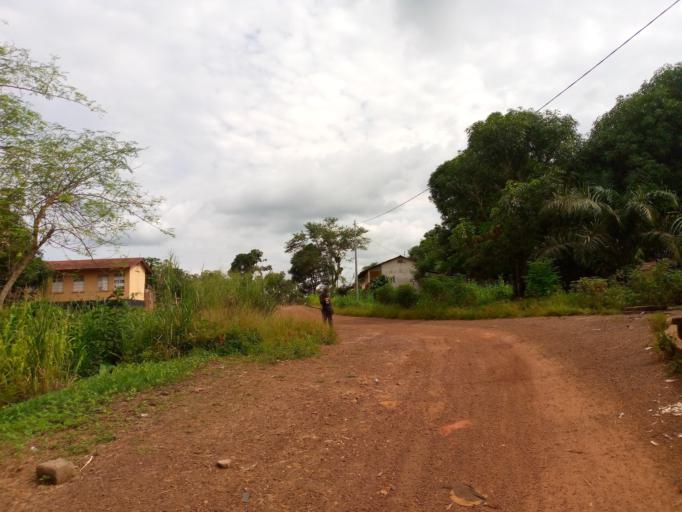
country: SL
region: Northern Province
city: Magburaka
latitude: 8.7224
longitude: -11.9391
